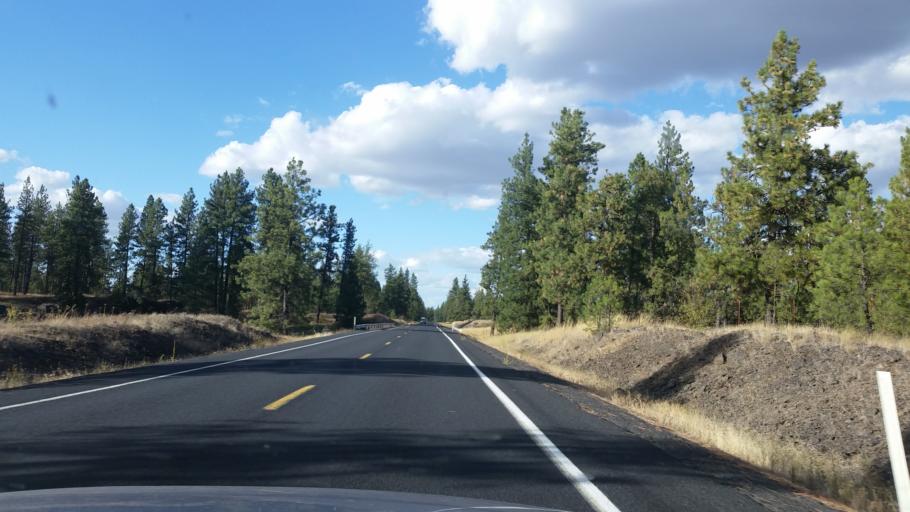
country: US
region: Washington
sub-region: Spokane County
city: Cheney
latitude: 47.4156
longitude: -117.5677
